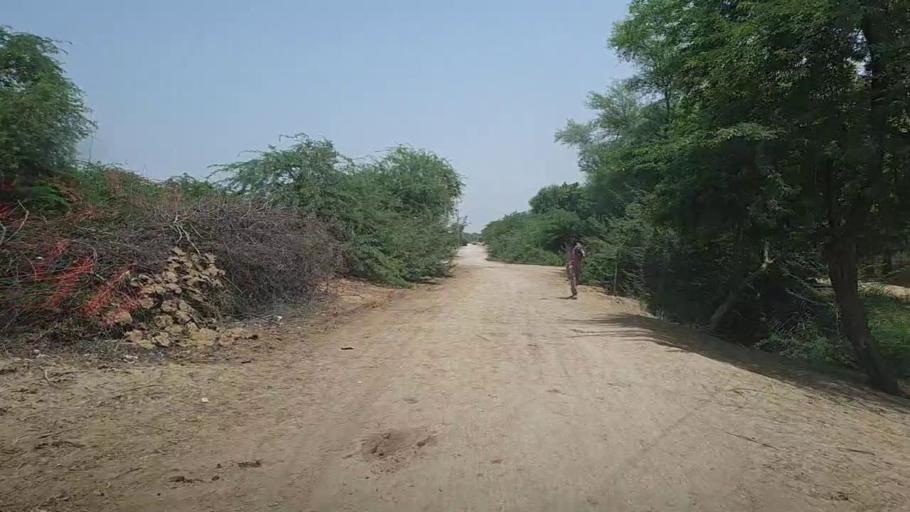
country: PK
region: Sindh
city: Pad Idan
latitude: 26.8454
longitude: 68.2909
